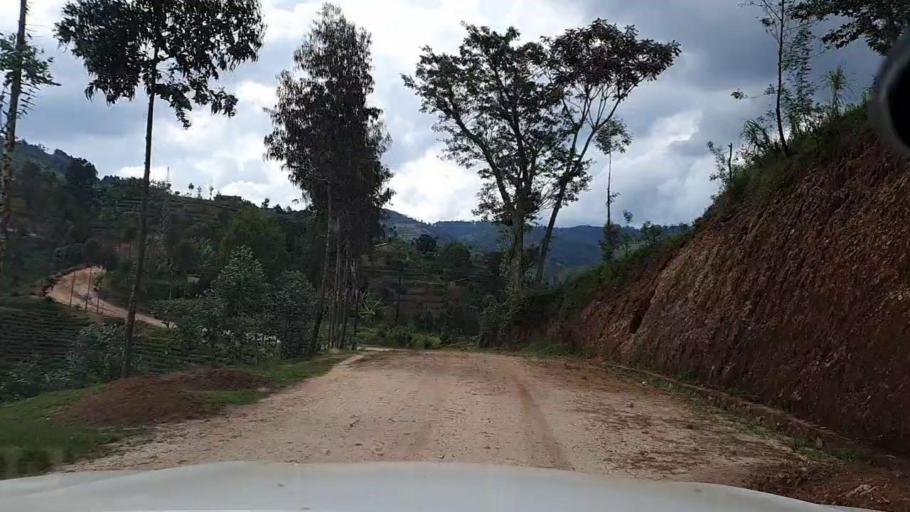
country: RW
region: Southern Province
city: Nzega
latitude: -2.7015
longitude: 29.4361
